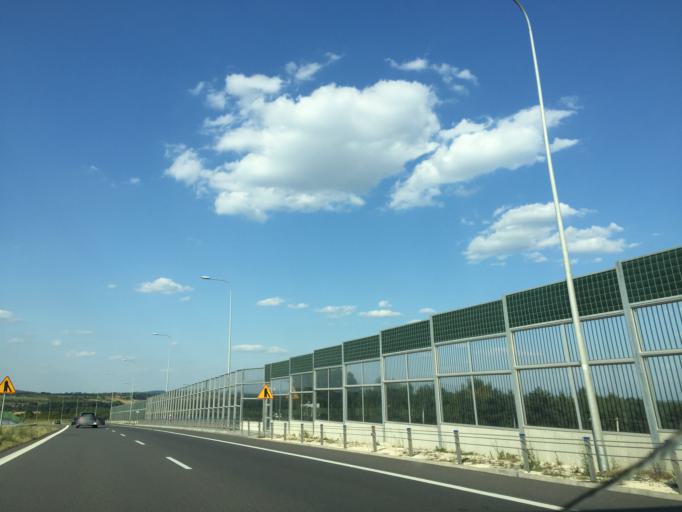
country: PL
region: Swietokrzyskie
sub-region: Powiat kielecki
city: Checiny
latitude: 50.7575
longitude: 20.4600
